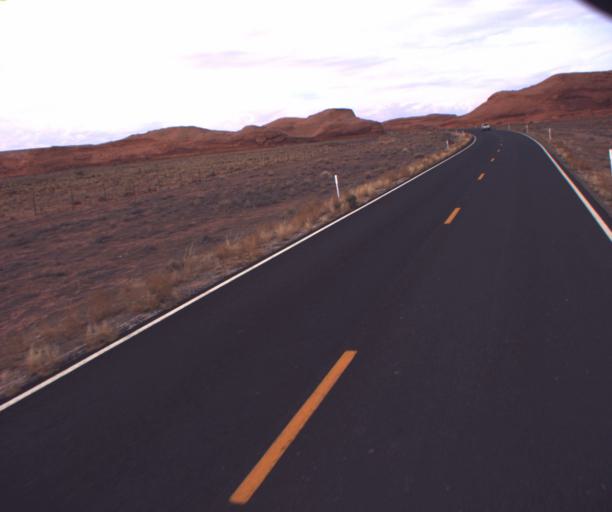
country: US
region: Arizona
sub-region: Apache County
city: Many Farms
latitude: 36.7641
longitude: -109.6521
